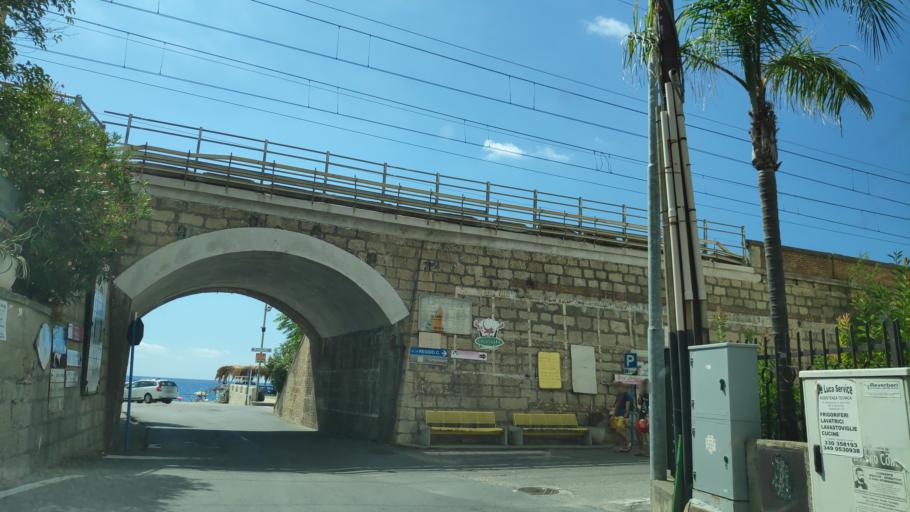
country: IT
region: Calabria
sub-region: Provincia di Cosenza
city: Belmonte Calabro
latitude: 39.1625
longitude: 16.0647
